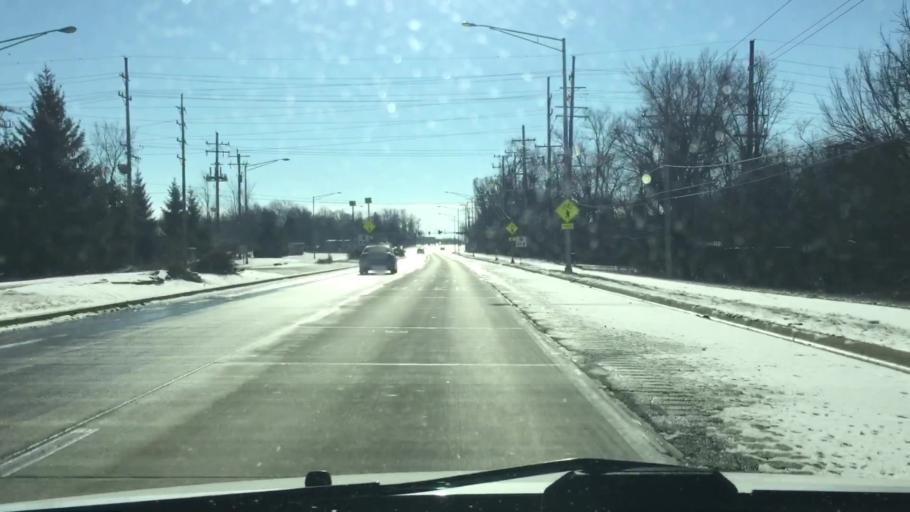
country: US
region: Illinois
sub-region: Kane County
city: Geneva
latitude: 41.8933
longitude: -88.2772
